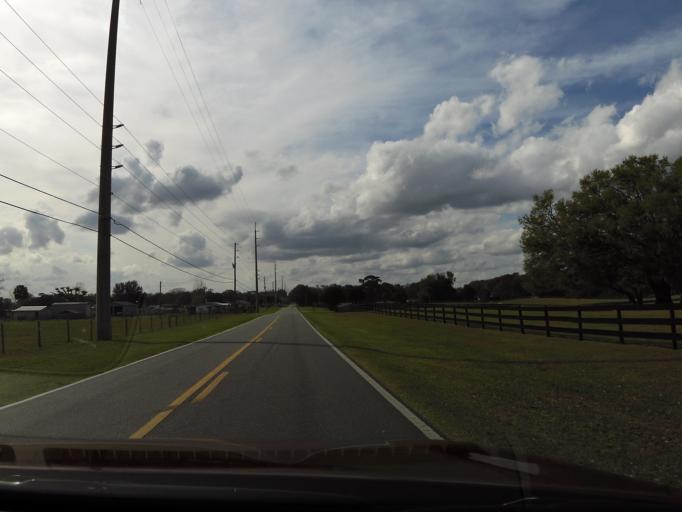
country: US
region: Florida
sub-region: Volusia County
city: De Leon Springs
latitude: 29.1371
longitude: -81.3313
